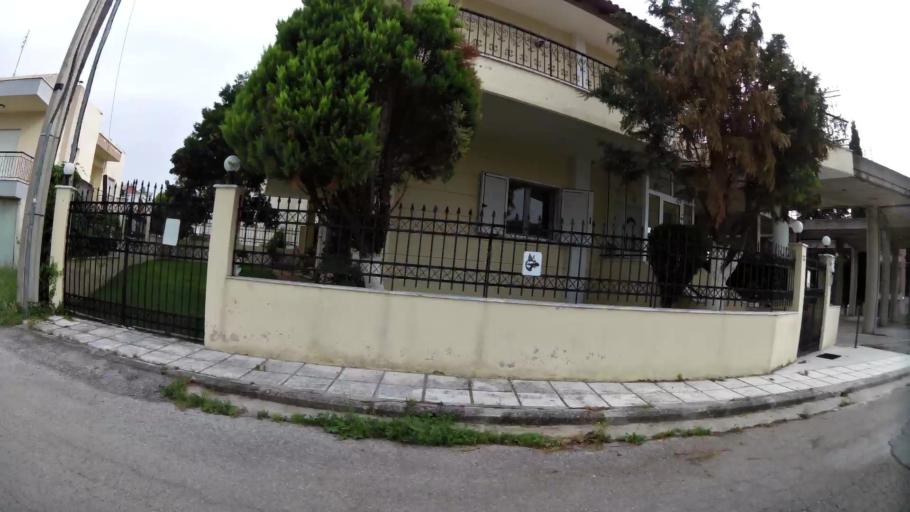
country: GR
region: Central Macedonia
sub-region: Nomos Thessalonikis
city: Oraiokastro
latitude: 40.7362
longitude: 22.9216
